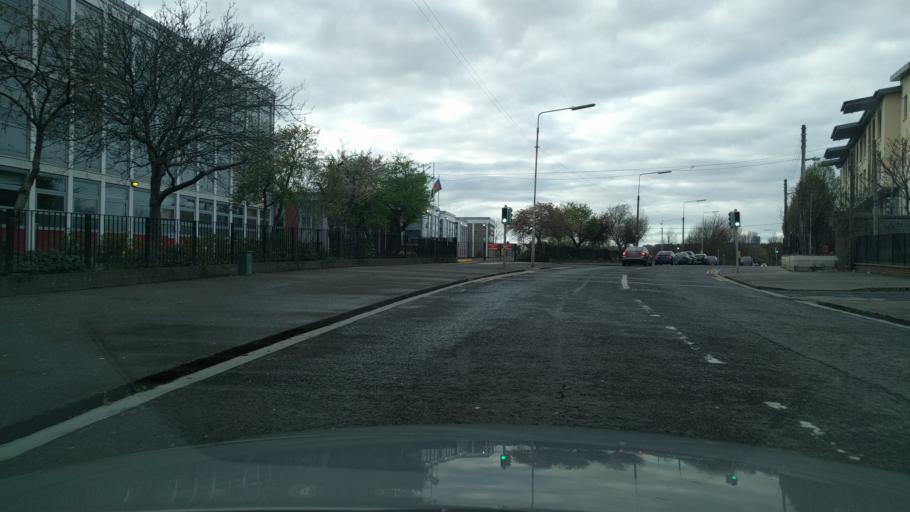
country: IE
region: Leinster
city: Chapelizod
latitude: 53.3447
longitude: -6.3506
